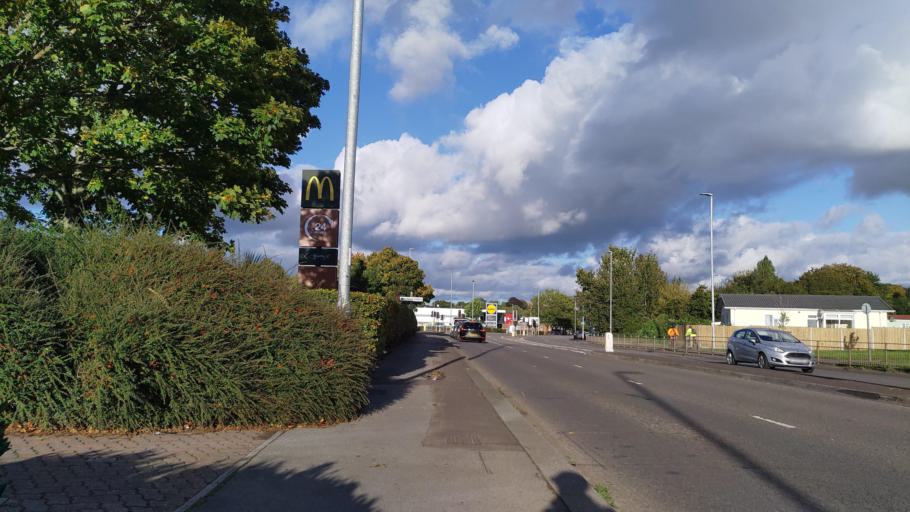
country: GB
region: England
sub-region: Somerset
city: Yeovil
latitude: 50.9354
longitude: -2.6450
